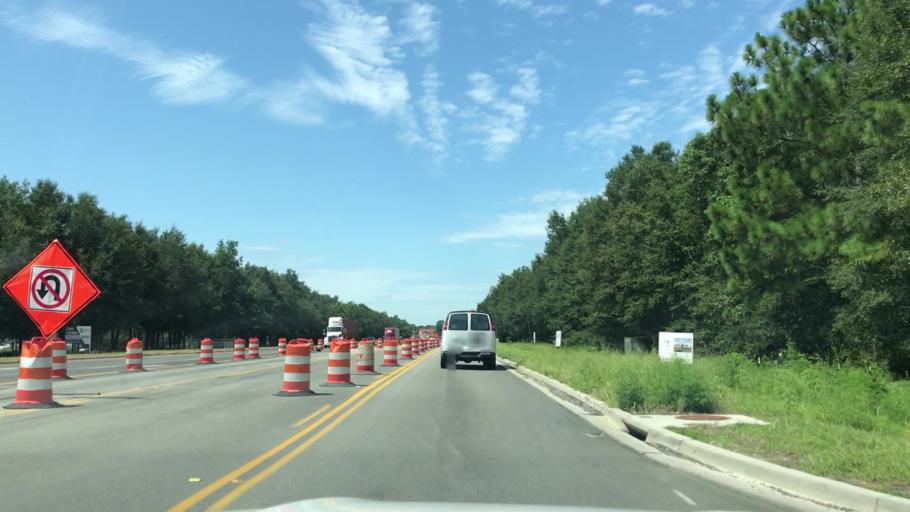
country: US
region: South Carolina
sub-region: Charleston County
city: North Charleston
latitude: 32.9061
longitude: -79.9076
